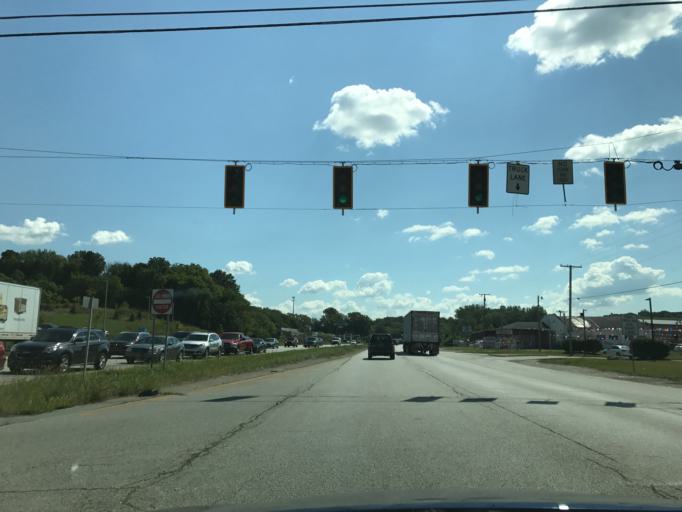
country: US
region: Indiana
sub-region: Porter County
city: Valparaiso
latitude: 41.4593
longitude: -87.0638
